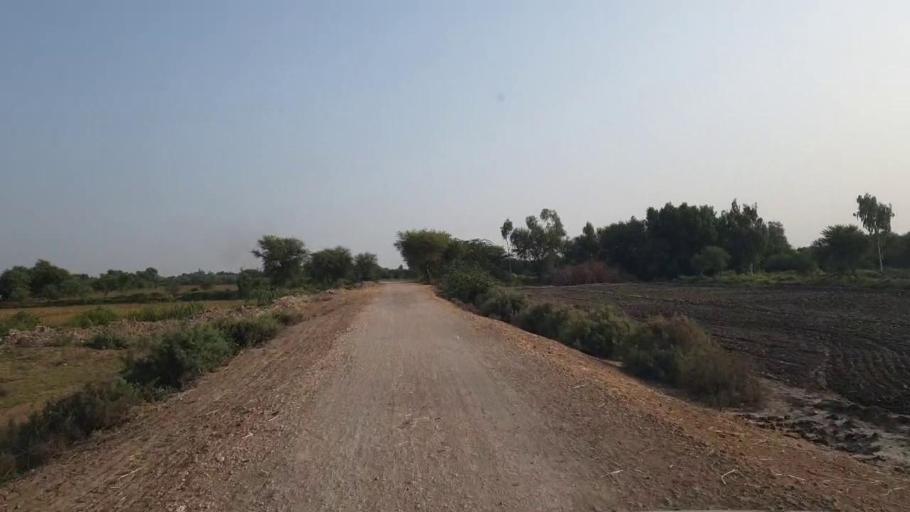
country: PK
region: Sindh
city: Rajo Khanani
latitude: 25.0394
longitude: 68.7689
